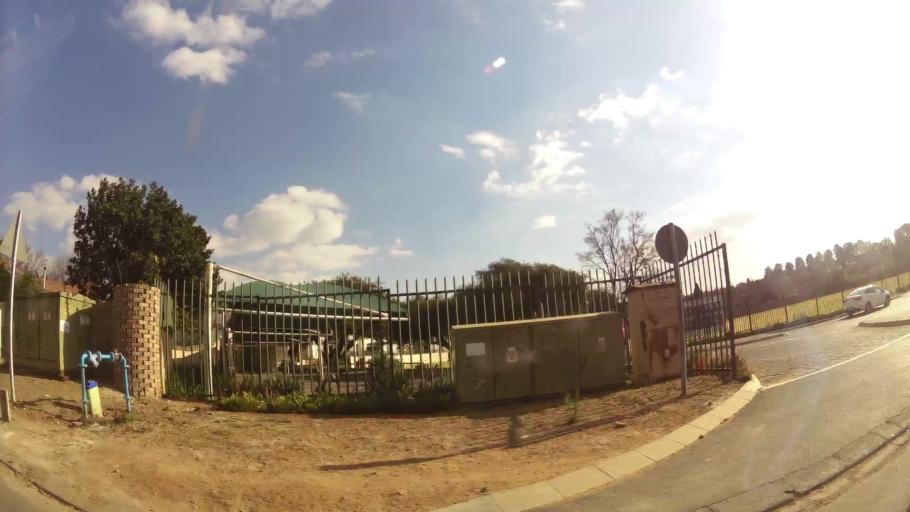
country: ZA
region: Gauteng
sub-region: City of Johannesburg Metropolitan Municipality
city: Diepsloot
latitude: -26.0138
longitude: 28.0314
